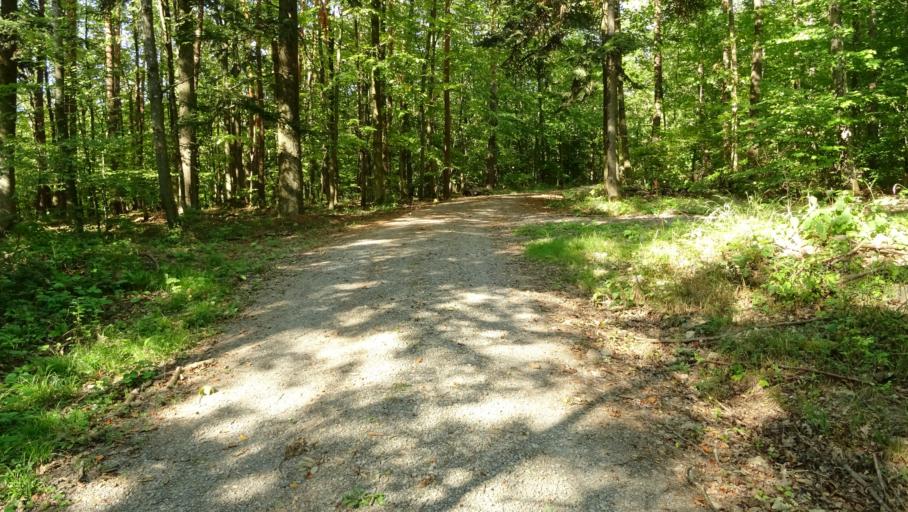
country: DE
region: Baden-Wuerttemberg
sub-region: Karlsruhe Region
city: Mosbach
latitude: 49.3851
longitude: 9.1253
